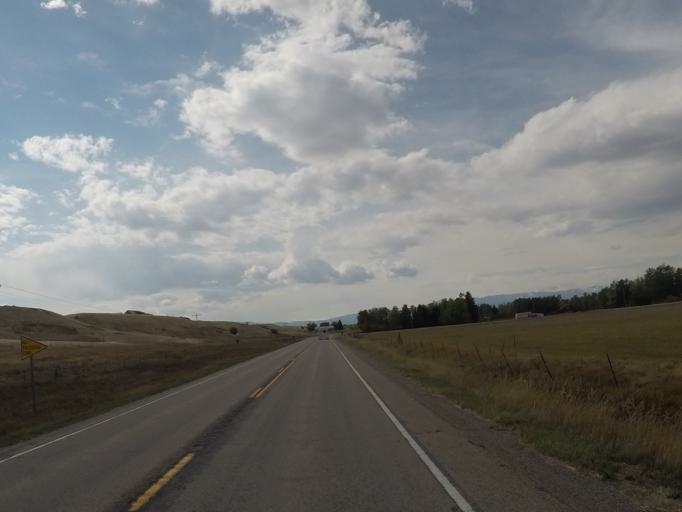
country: US
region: Montana
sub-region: Carbon County
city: Red Lodge
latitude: 45.3887
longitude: -109.1350
